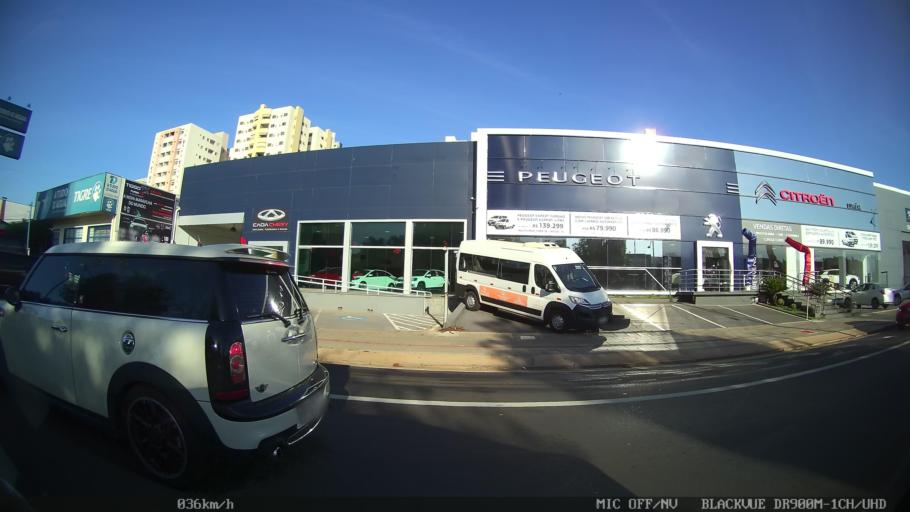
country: BR
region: Sao Paulo
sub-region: Sao Jose Do Rio Preto
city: Sao Jose do Rio Preto
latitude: -20.8205
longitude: -49.3981
